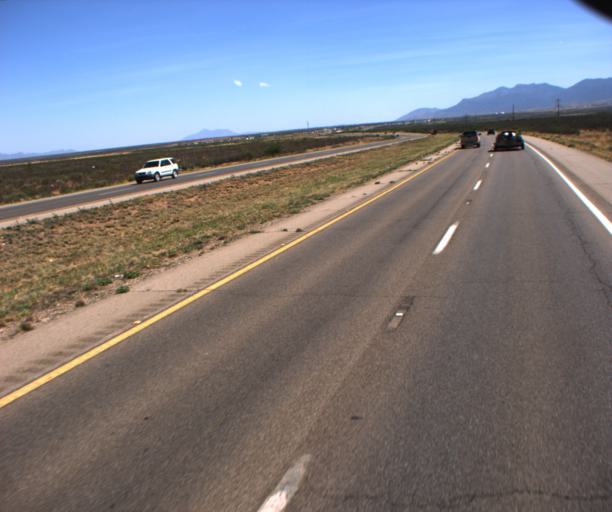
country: US
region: Arizona
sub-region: Cochise County
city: Huachuca City
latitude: 31.6627
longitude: -110.3502
